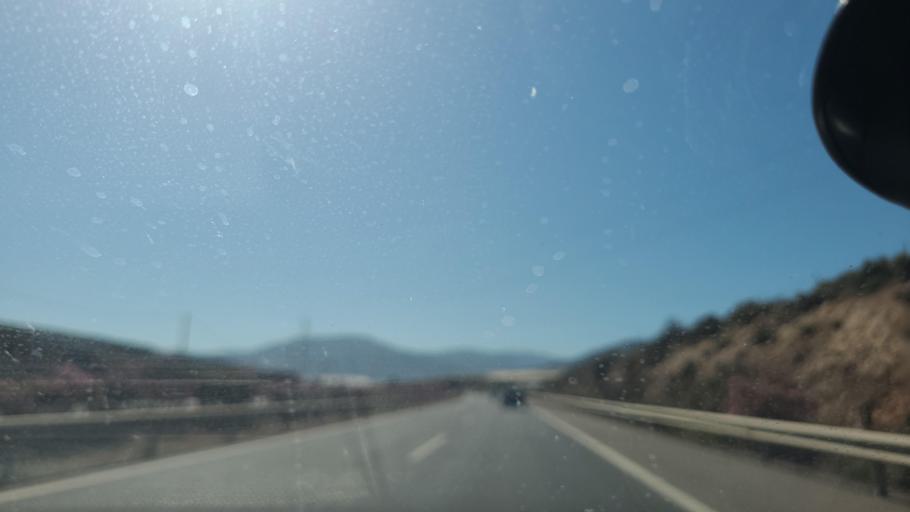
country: ES
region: Andalusia
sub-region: Provincia de Almeria
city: Adra
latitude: 36.7598
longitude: -2.9401
